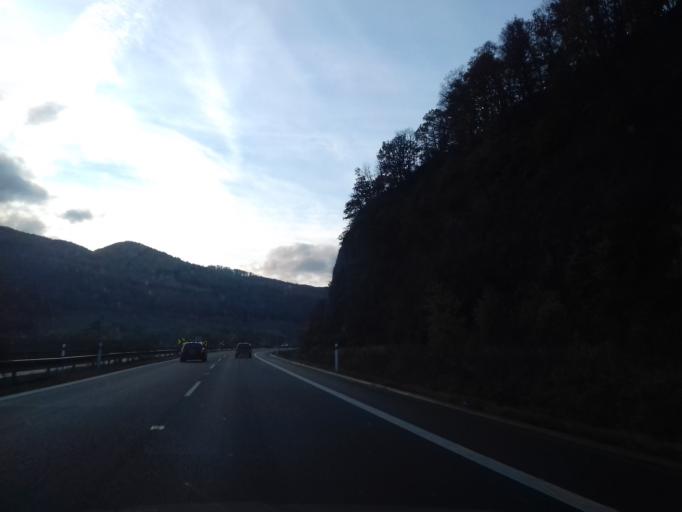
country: SK
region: Banskobystricky
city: Zarnovica
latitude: 48.4461
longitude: 18.6956
